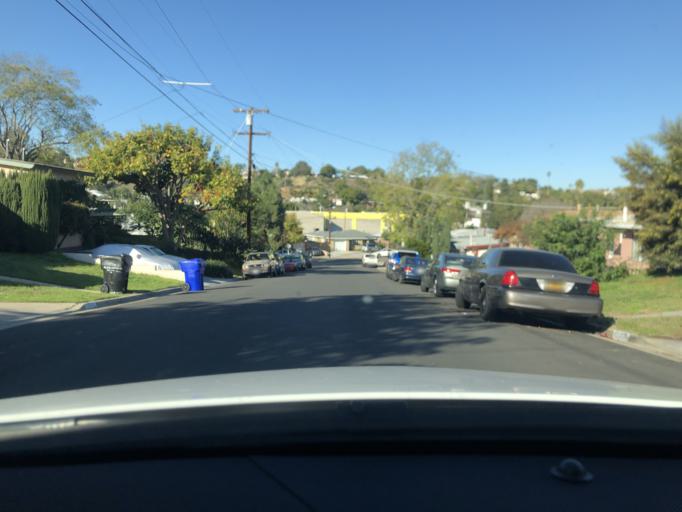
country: US
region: California
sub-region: San Diego County
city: Lemon Grove
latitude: 32.7504
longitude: -117.0661
